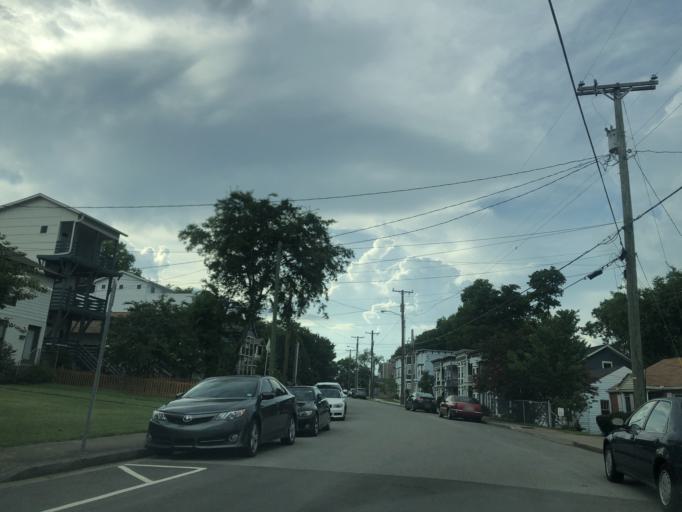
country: US
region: Tennessee
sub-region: Davidson County
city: Nashville
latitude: 36.1836
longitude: -86.7951
